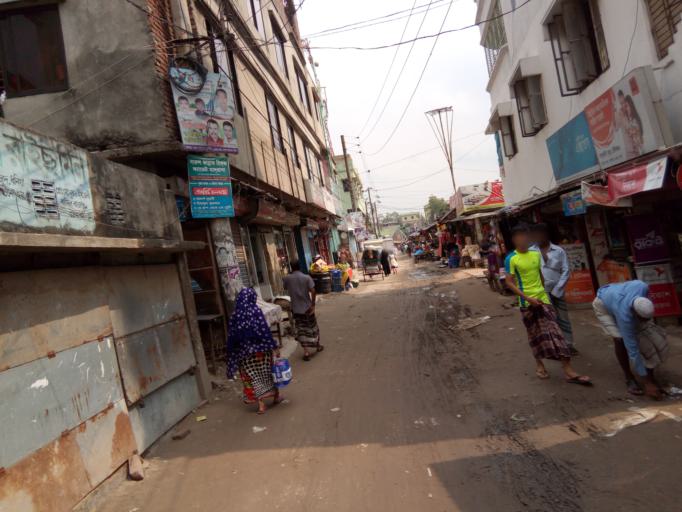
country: BD
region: Dhaka
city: Paltan
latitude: 23.7174
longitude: 90.4847
